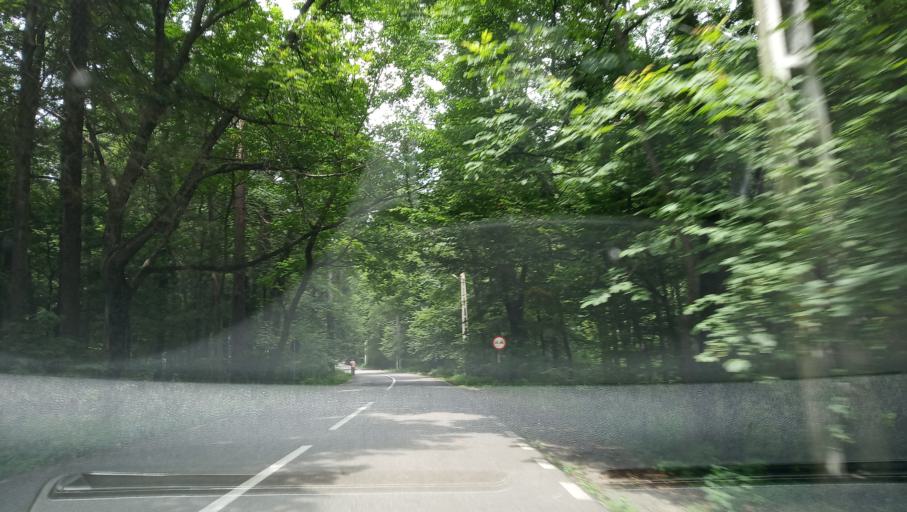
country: RO
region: Gorj
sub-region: Comuna Tismana
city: Pocruia
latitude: 45.0780
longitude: 22.9300
